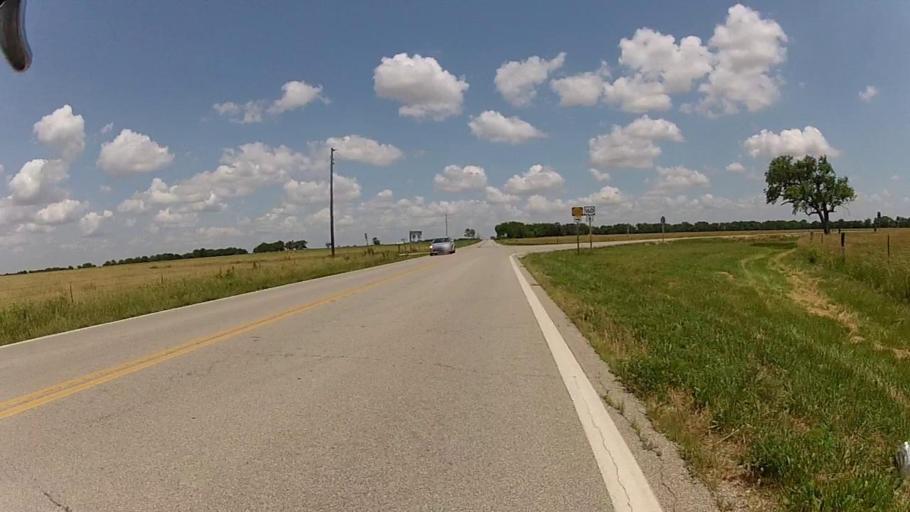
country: US
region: Kansas
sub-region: Labette County
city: Altamont
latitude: 37.1925
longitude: -95.3589
